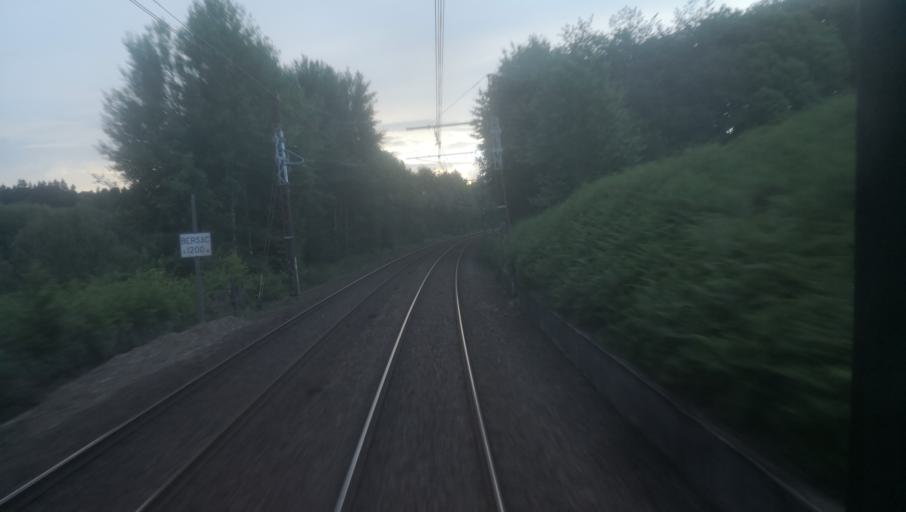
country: FR
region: Limousin
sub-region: Departement de la Haute-Vienne
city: Bessines-sur-Gartempe
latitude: 46.0727
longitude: 1.4299
